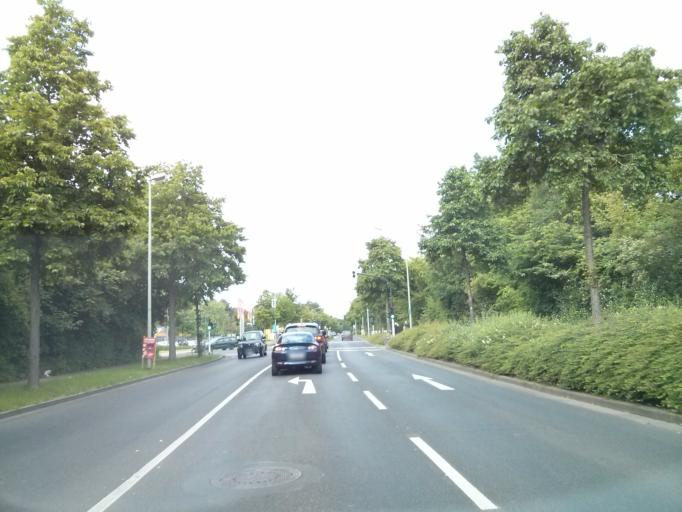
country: DE
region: North Rhine-Westphalia
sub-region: Regierungsbezirk Dusseldorf
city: Krefeld
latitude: 51.3440
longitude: 6.5377
